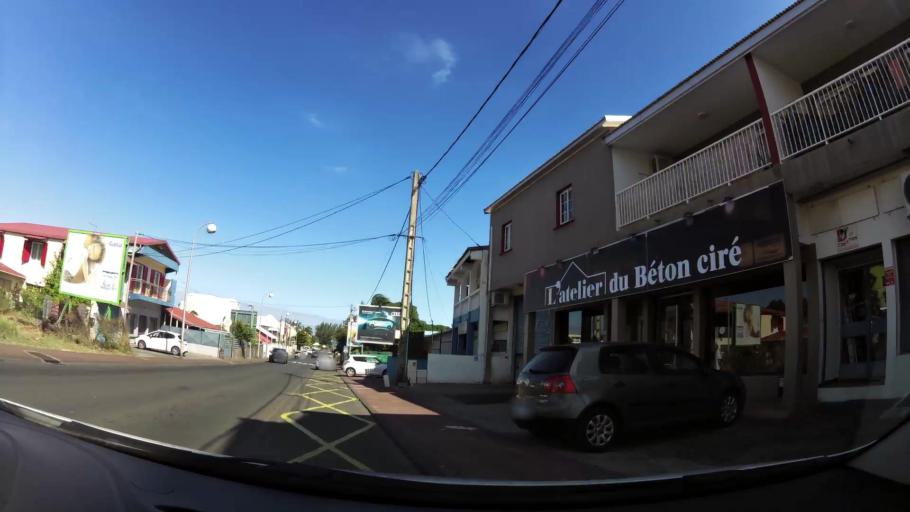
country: RE
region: Reunion
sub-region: Reunion
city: Saint-Pierre
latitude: -21.3359
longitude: 55.4595
